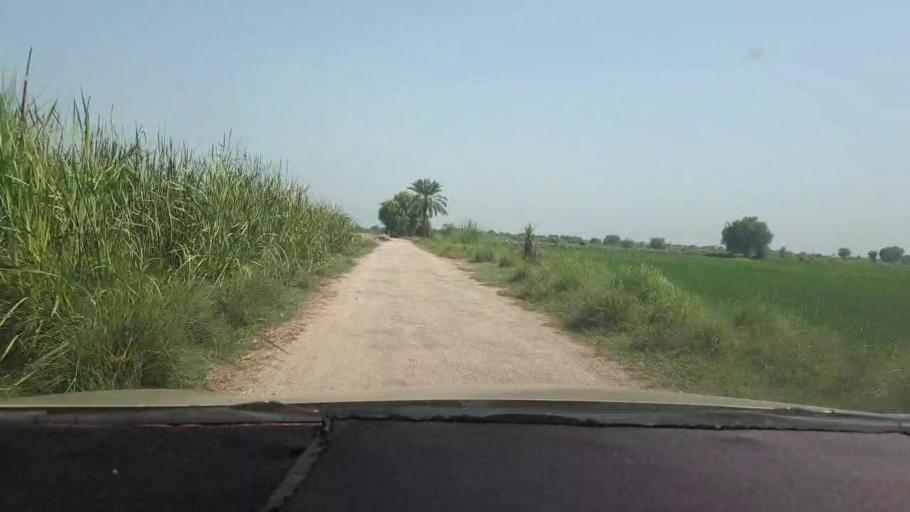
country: PK
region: Sindh
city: Miro Khan
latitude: 27.6986
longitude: 68.0931
